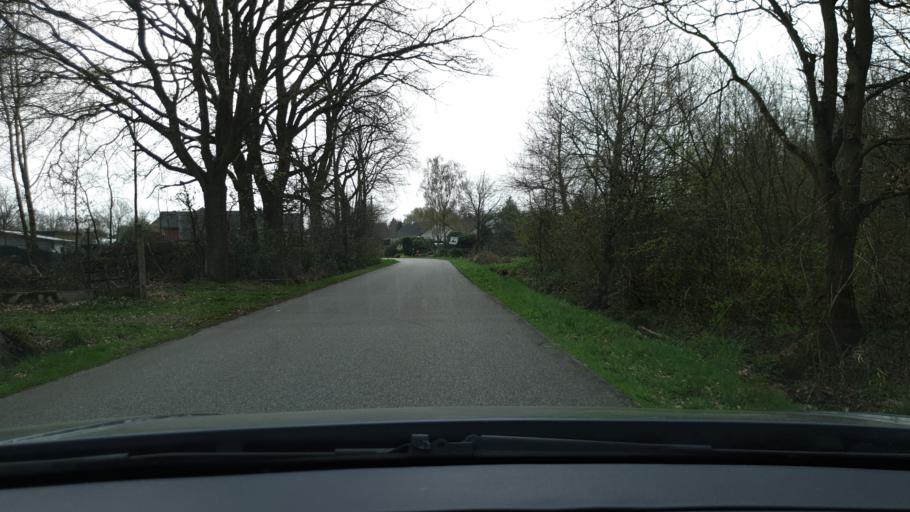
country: BE
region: Flanders
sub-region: Provincie Antwerpen
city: Geel
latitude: 51.1301
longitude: 4.9983
